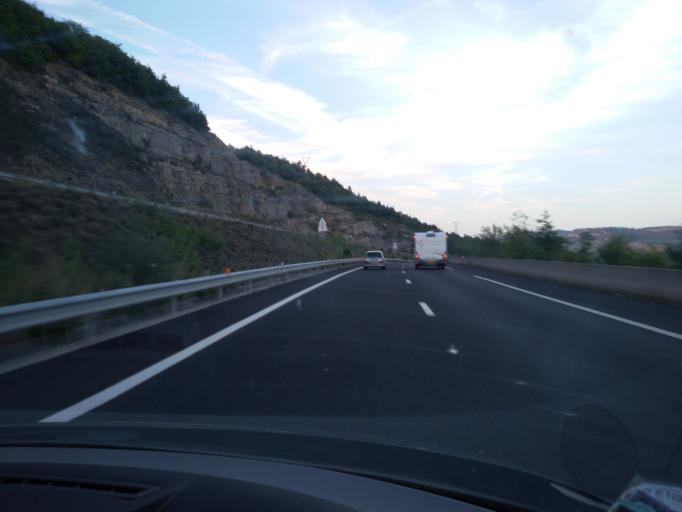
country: FR
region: Languedoc-Roussillon
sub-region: Departement de la Lozere
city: Chirac
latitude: 44.4931
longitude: 3.2241
